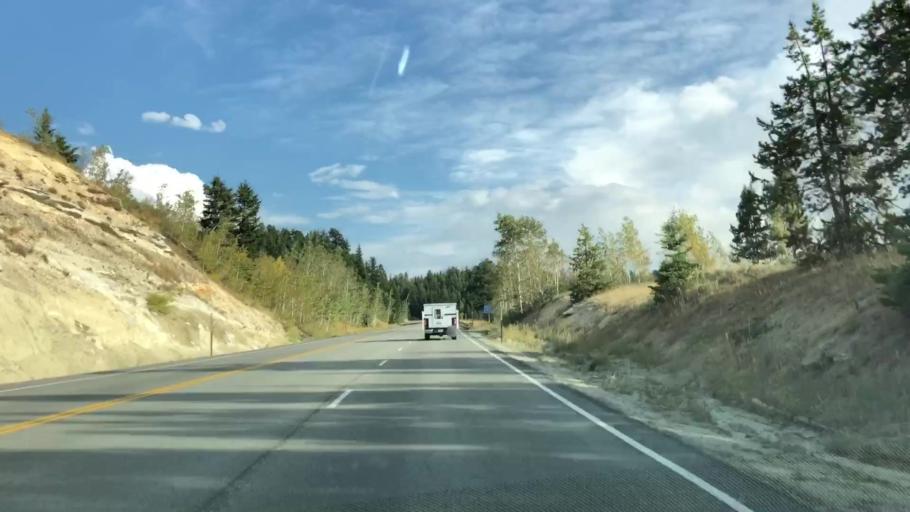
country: US
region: Wyoming
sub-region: Sublette County
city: Pinedale
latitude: 43.1367
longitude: -110.2082
